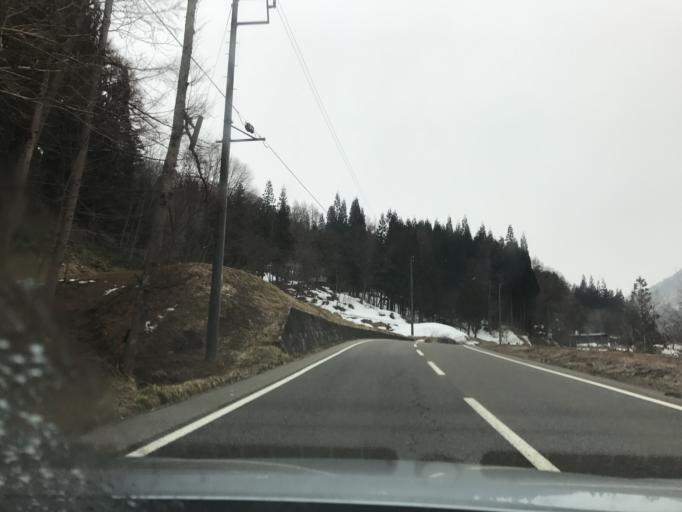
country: JP
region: Nagano
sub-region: Kitaazumi Gun
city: Hakuba
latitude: 36.6017
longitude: 137.8887
